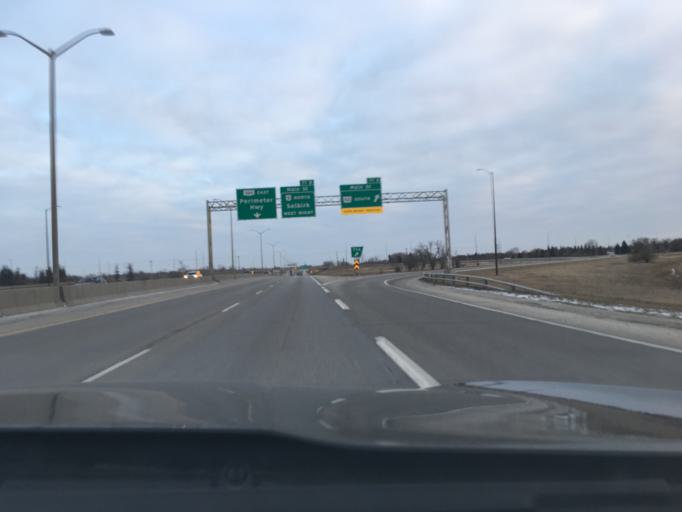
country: CA
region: Manitoba
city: Winnipeg
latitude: 49.9744
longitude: -97.0791
